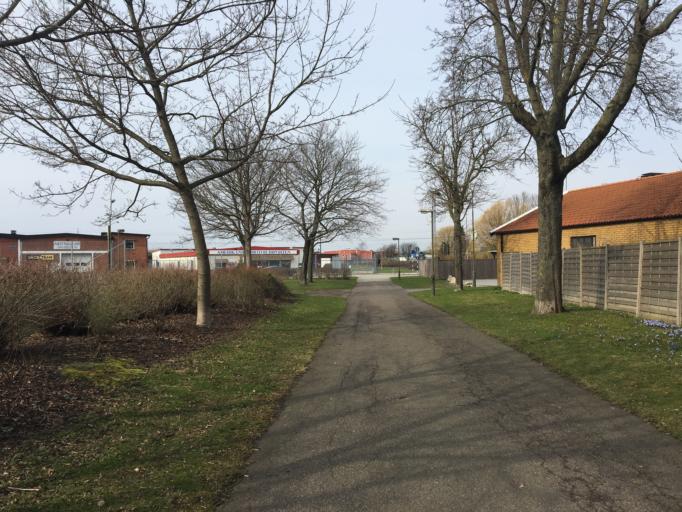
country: SE
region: Skane
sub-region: Burlovs Kommun
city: Arloev
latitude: 55.6389
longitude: 13.0803
